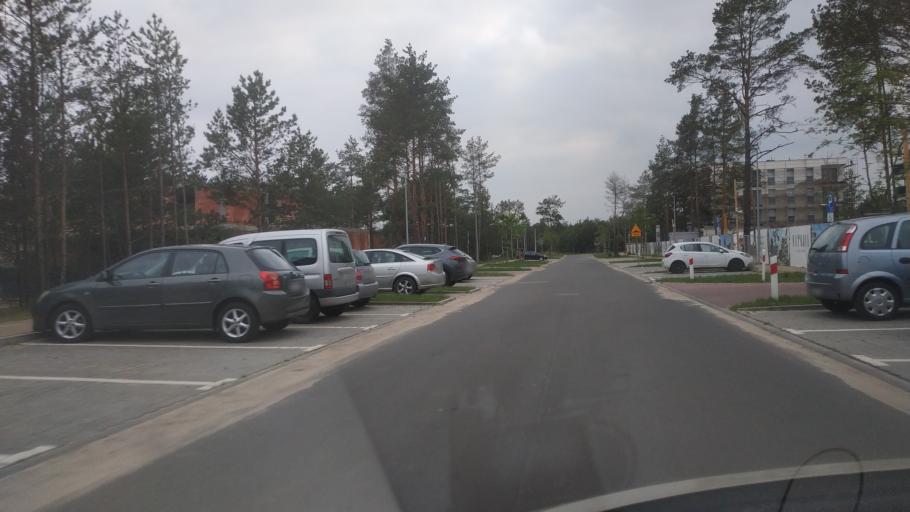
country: PL
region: Kujawsko-Pomorskie
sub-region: Torun
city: Torun
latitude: 53.0506
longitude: 18.6028
